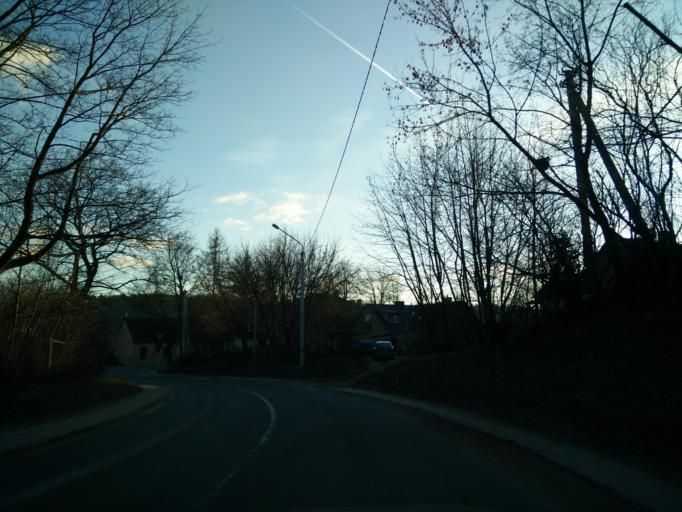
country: LT
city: Skaidiskes
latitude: 54.6958
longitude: 25.3972
